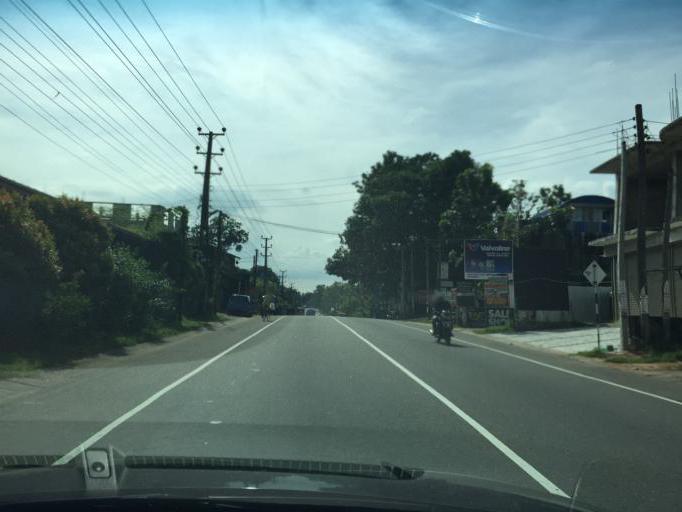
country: LK
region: Western
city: Horana South
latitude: 6.7223
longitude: 80.0773
